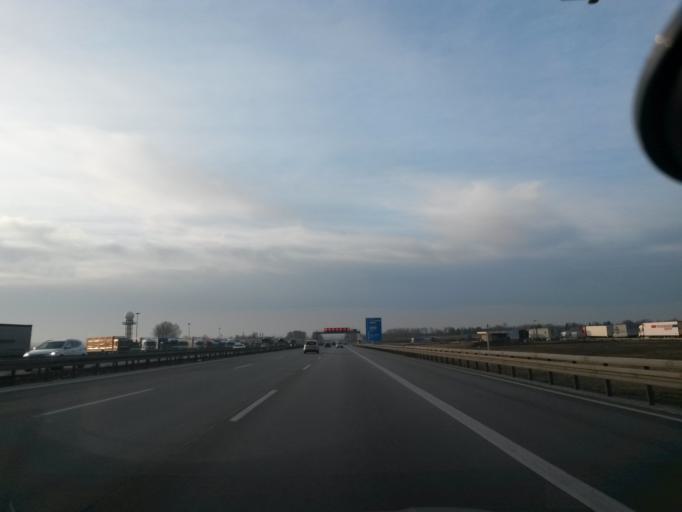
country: DE
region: Bavaria
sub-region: Upper Bavaria
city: Eching
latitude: 48.3388
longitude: 11.6082
